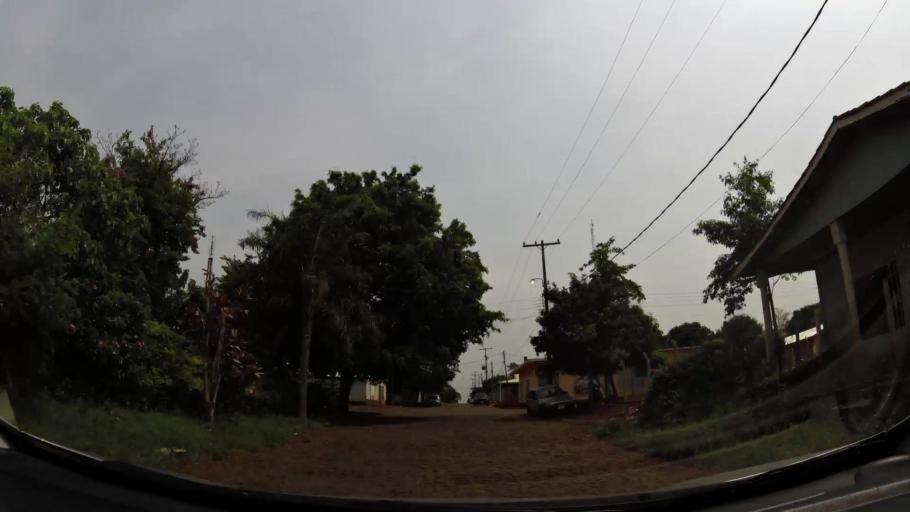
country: BR
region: Parana
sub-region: Foz Do Iguacu
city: Foz do Iguacu
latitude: -25.5693
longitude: -54.6093
